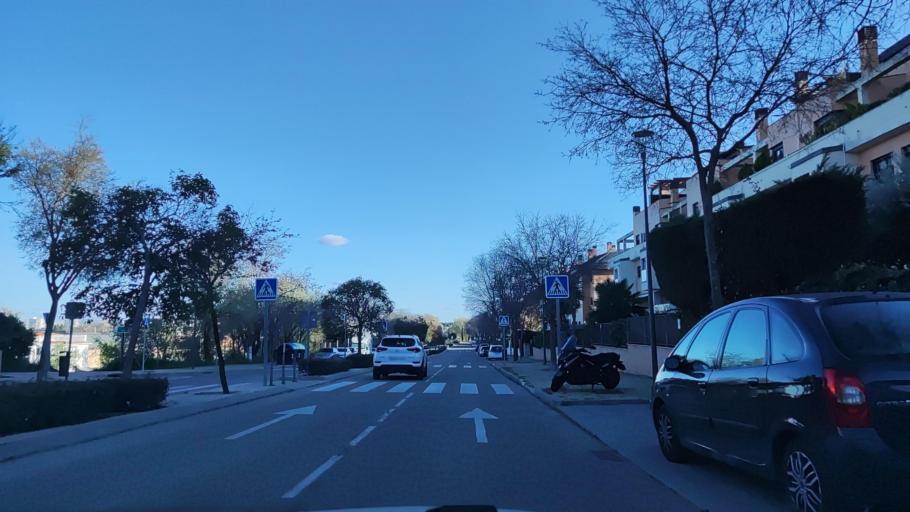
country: ES
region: Madrid
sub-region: Provincia de Madrid
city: Pozuelo de Alarcon
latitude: 40.4080
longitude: -3.7822
